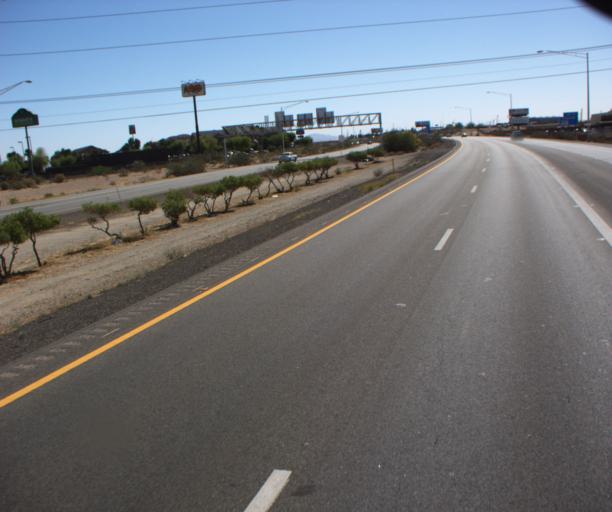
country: US
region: Arizona
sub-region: Yuma County
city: Yuma
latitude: 32.6958
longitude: -114.6060
